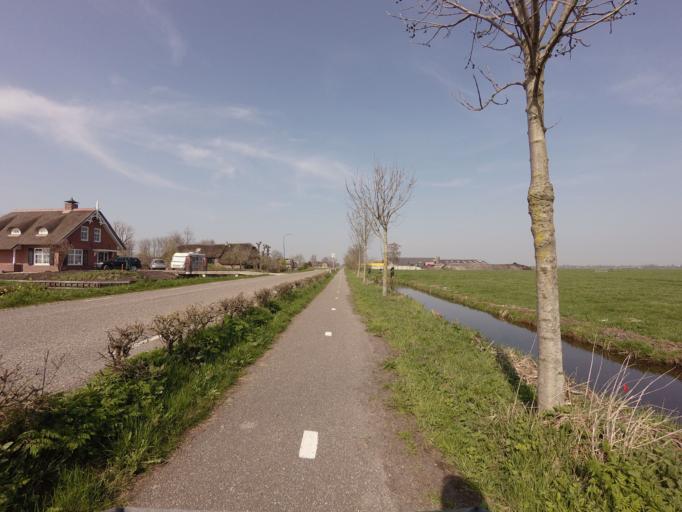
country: NL
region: Utrecht
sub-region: Stichtse Vecht
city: Breukelen
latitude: 52.1458
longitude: 4.9747
